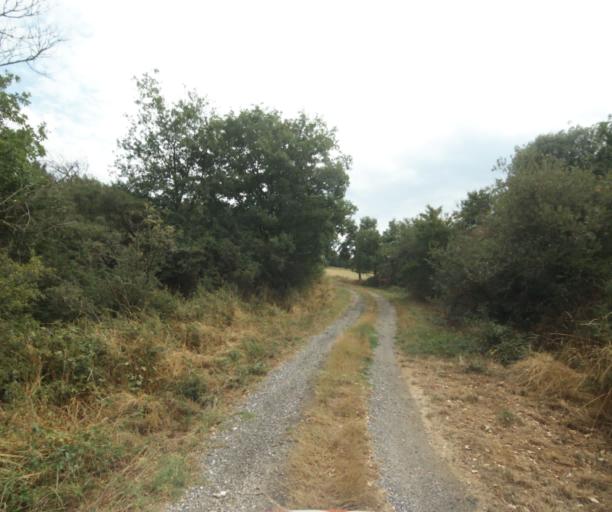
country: FR
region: Midi-Pyrenees
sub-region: Departement de la Haute-Garonne
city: Revel
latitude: 43.4400
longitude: 1.9765
